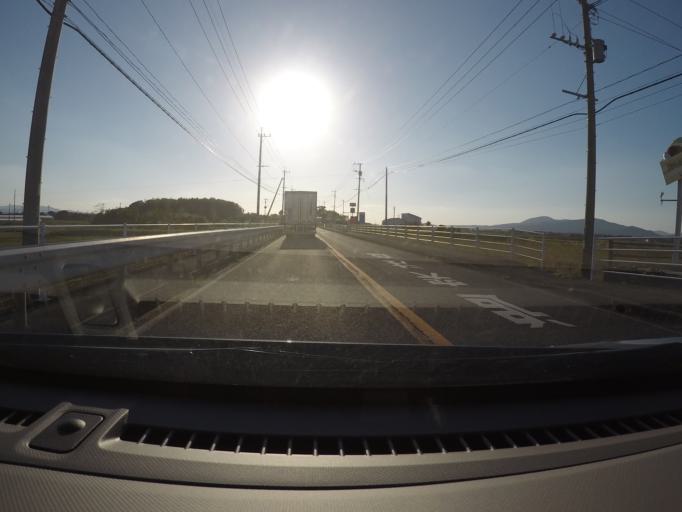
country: JP
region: Kagoshima
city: Izumi
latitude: 32.1065
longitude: 130.3200
